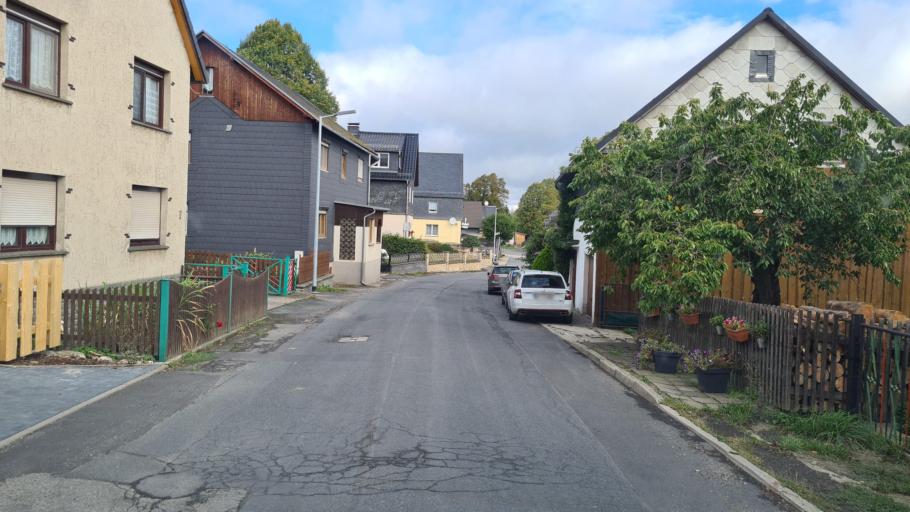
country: DE
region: Thuringia
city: Probstzella
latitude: 50.5639
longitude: 11.4066
